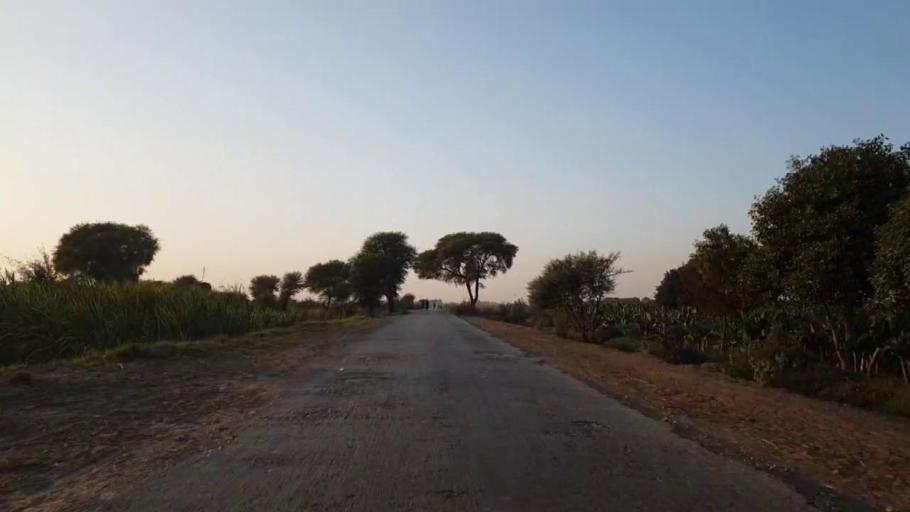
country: PK
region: Sindh
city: Chambar
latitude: 25.2501
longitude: 68.6770
